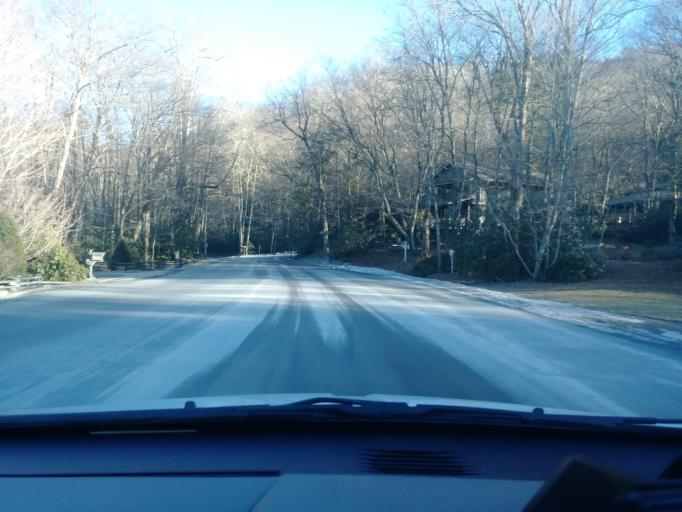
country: US
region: North Carolina
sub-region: Avery County
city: Banner Elk
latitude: 36.1287
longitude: -81.8544
